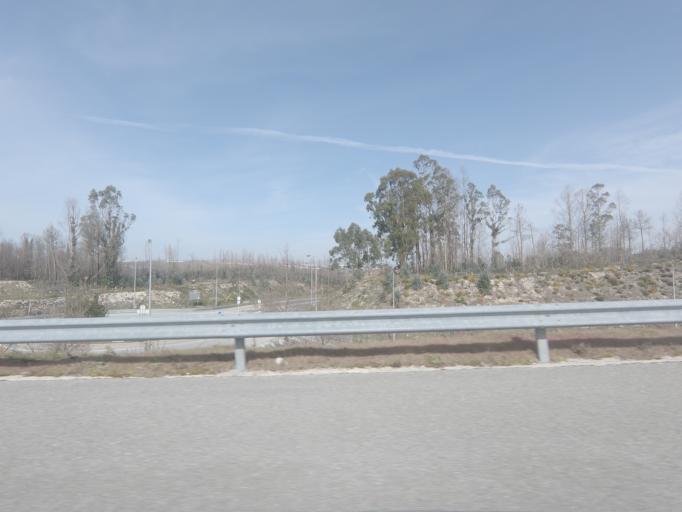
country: PT
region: Viseu
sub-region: Oliveira de Frades
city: Oliveira de Frades
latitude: 40.6830
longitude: -8.1994
